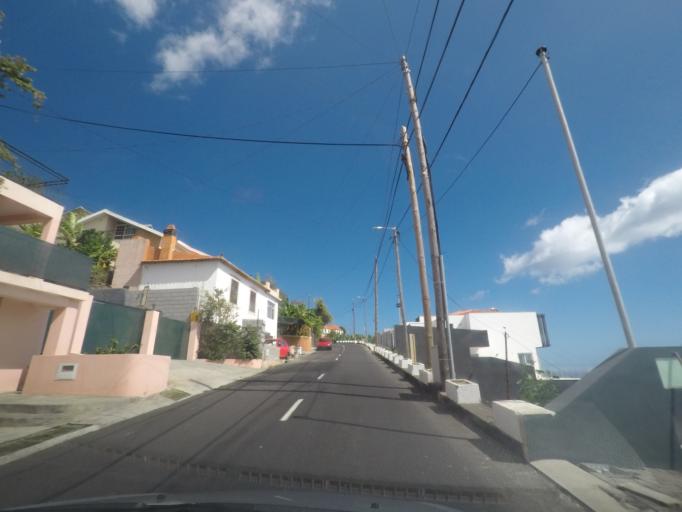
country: PT
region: Madeira
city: Ribeira Brava
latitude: 32.6704
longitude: -17.0598
